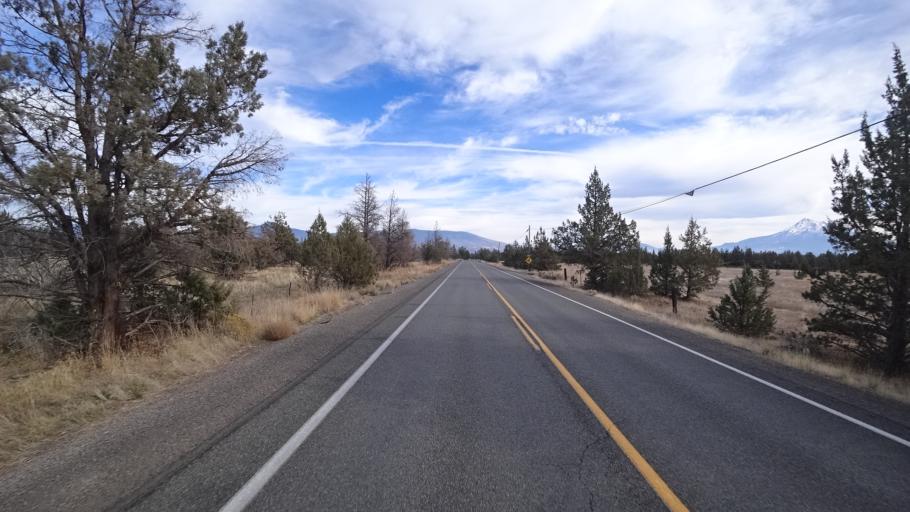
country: US
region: California
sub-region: Siskiyou County
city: Montague
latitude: 41.6347
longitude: -122.4415
